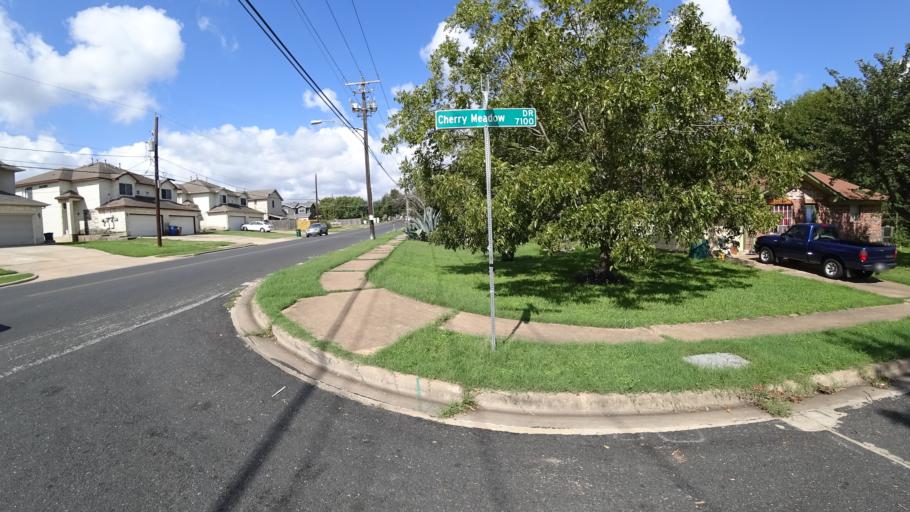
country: US
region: Texas
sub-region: Travis County
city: Manchaca
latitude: 30.1988
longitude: -97.8046
